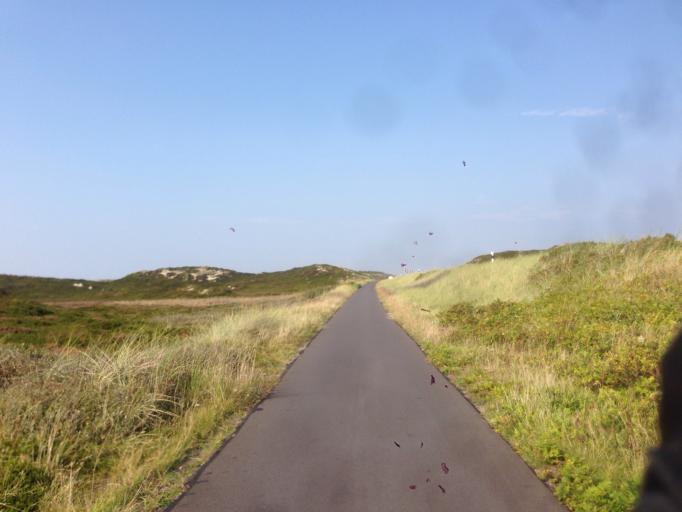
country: DE
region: Schleswig-Holstein
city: Westerland
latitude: 54.8353
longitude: 8.2916
